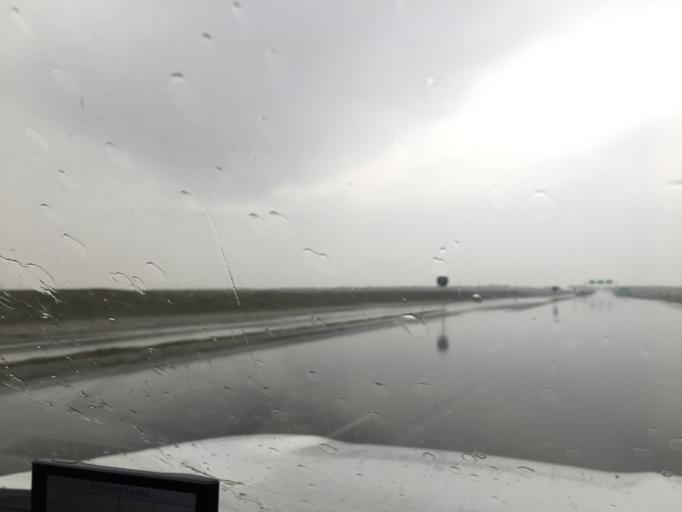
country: TM
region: Ahal
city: Annau
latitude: 37.8426
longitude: 58.7188
